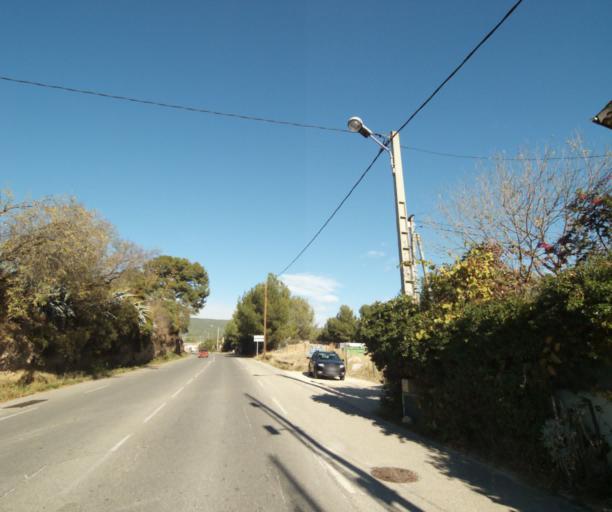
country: FR
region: Provence-Alpes-Cote d'Azur
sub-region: Departement des Bouches-du-Rhone
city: Ceyreste
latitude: 43.2059
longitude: 5.6271
